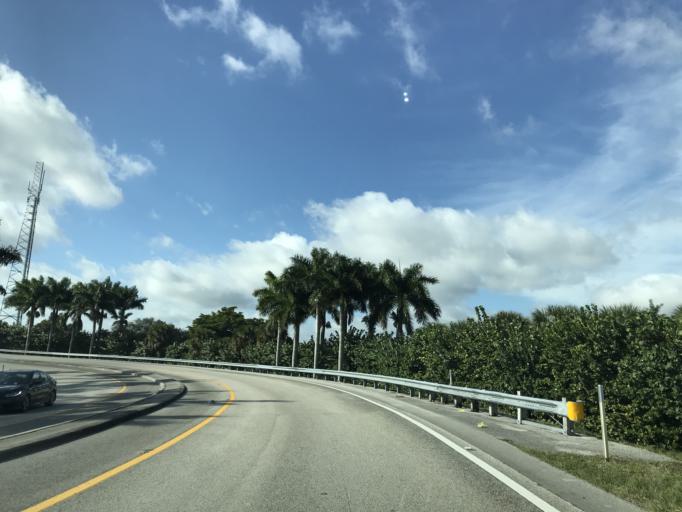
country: US
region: Florida
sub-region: Palm Beach County
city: Boca Del Mar
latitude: 26.3760
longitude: -80.1722
